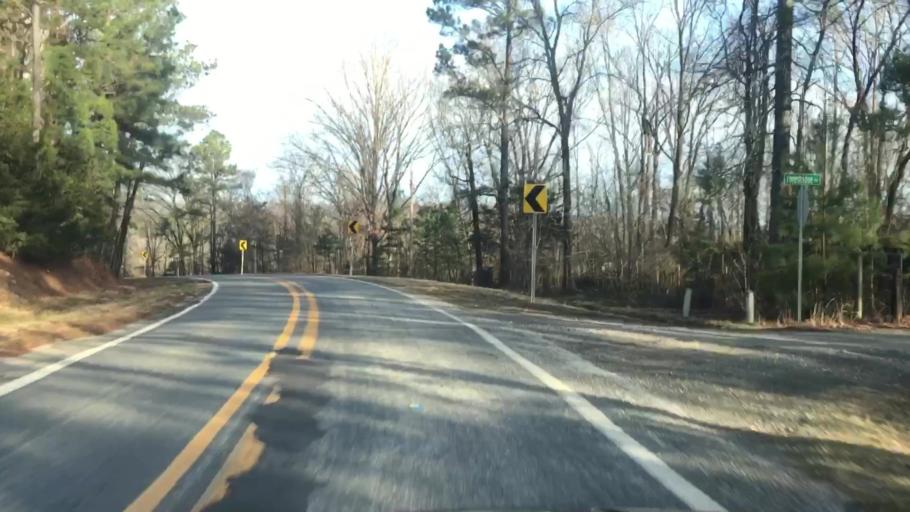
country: US
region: Arkansas
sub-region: Garland County
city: Rockwell
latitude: 34.4870
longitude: -93.2734
